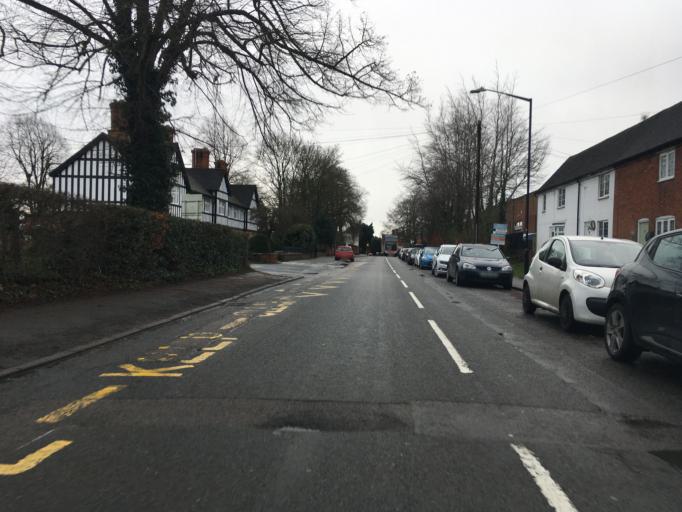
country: GB
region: England
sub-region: Warwickshire
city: Alcester
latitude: 52.2181
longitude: -1.8759
